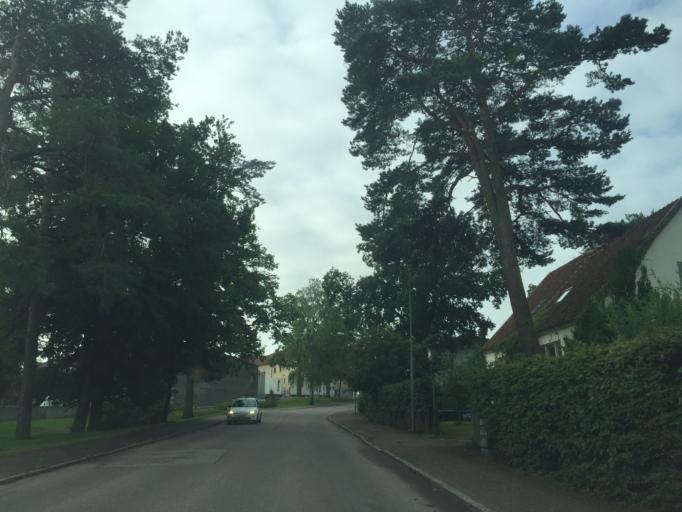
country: SE
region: Skane
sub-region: Angelholms Kommun
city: AEngelholm
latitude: 56.2413
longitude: 12.8574
